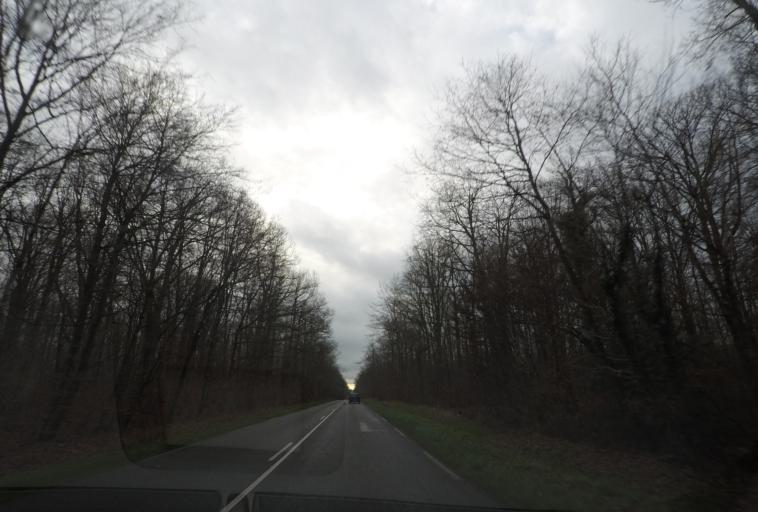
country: FR
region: Pays de la Loire
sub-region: Departement de la Sarthe
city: Vibraye
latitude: 48.0316
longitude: 0.7475
